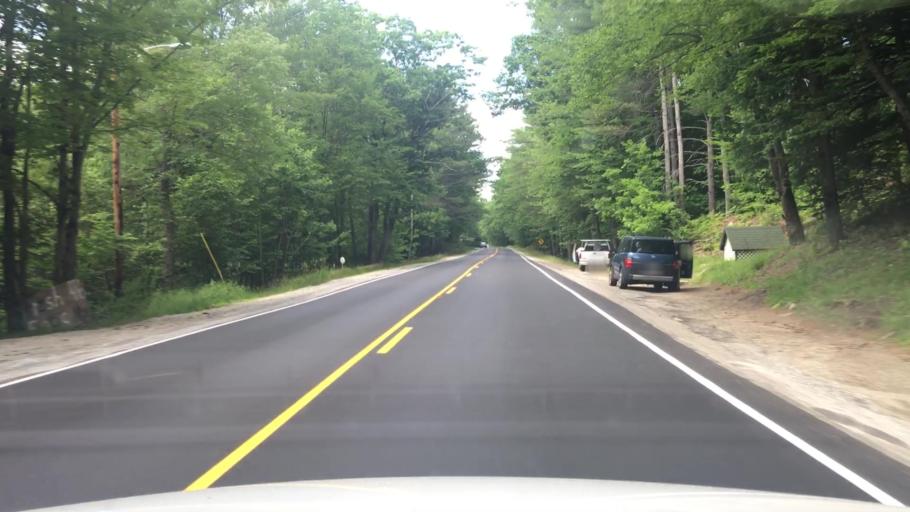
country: US
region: Maine
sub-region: Oxford County
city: West Paris
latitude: 44.3906
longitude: -70.6602
